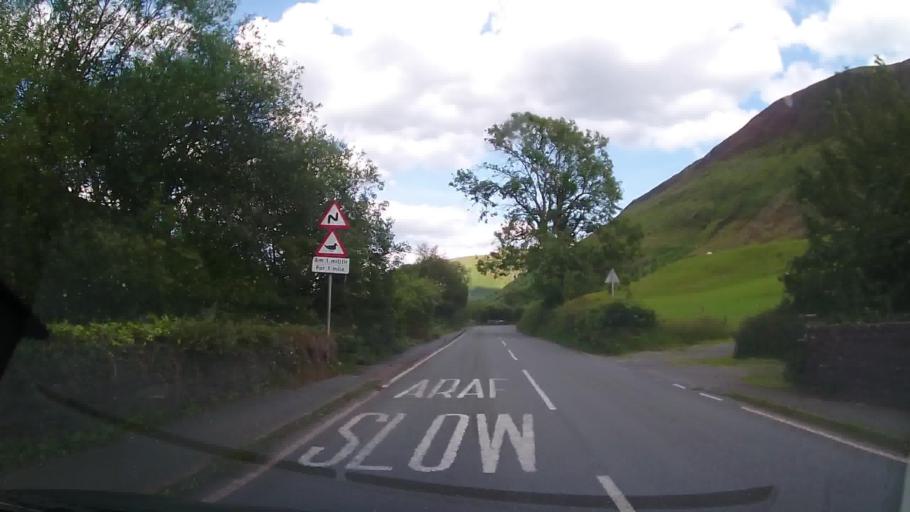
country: GB
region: Wales
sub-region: Gwynedd
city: Corris
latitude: 52.6672
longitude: -3.9077
